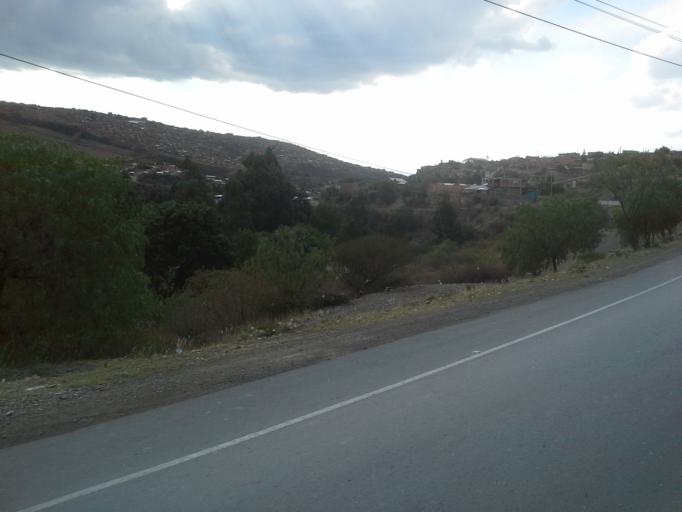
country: BO
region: Cochabamba
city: Cochabamba
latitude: -17.4854
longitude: -66.0989
